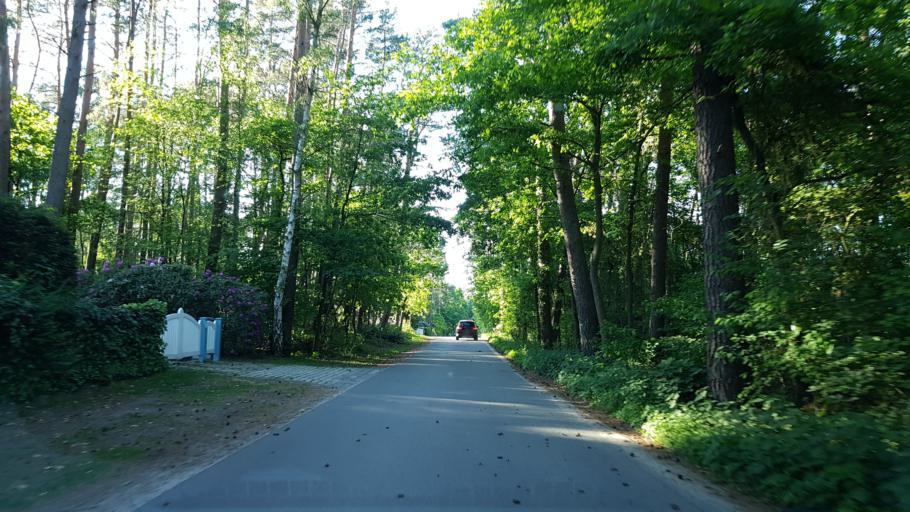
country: DE
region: Lower Saxony
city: Stelle
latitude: 53.3538
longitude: 10.1058
